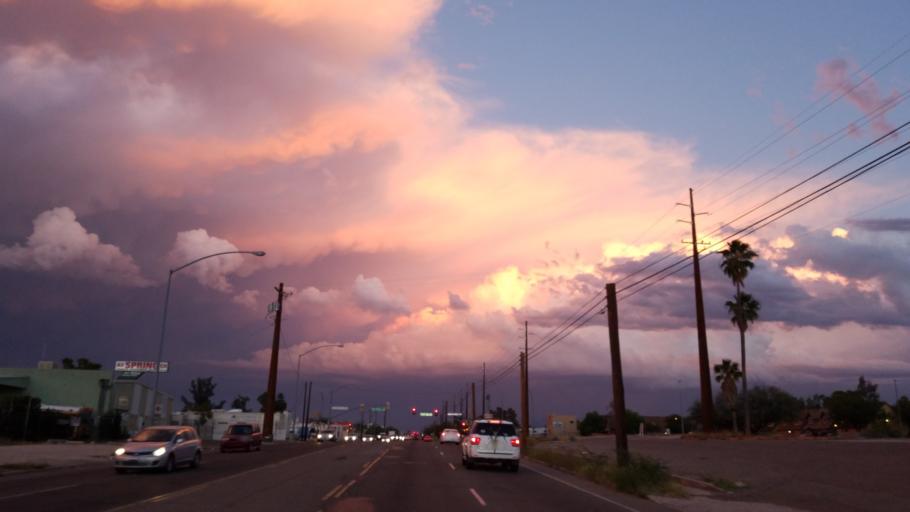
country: US
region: Arizona
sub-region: Pima County
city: South Tucson
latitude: 32.2503
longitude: -110.9692
